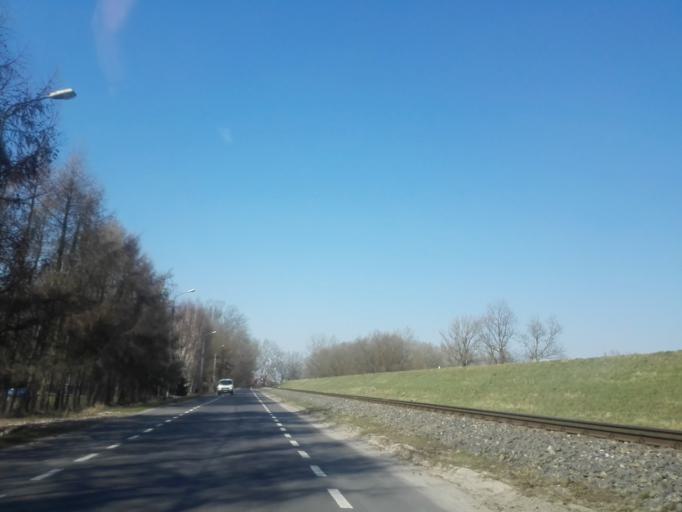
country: PL
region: Masovian Voivodeship
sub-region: Warszawa
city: Wilanow
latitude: 52.1659
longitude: 21.1272
